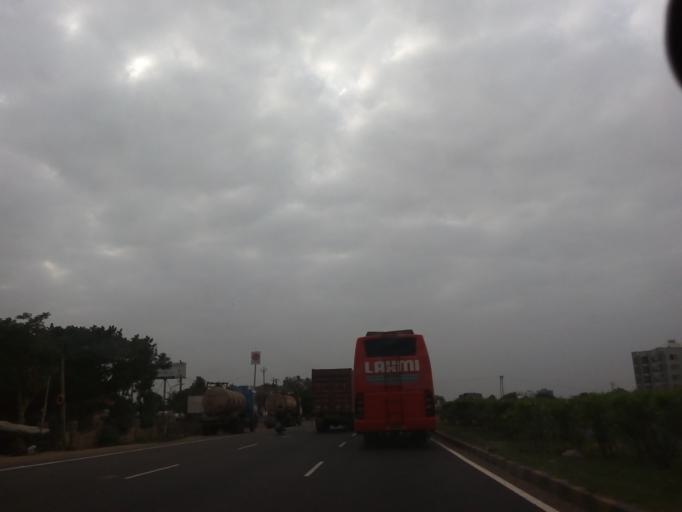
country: IN
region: Gujarat
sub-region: Vadodara
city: Vadodara
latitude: 22.3593
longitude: 73.2081
